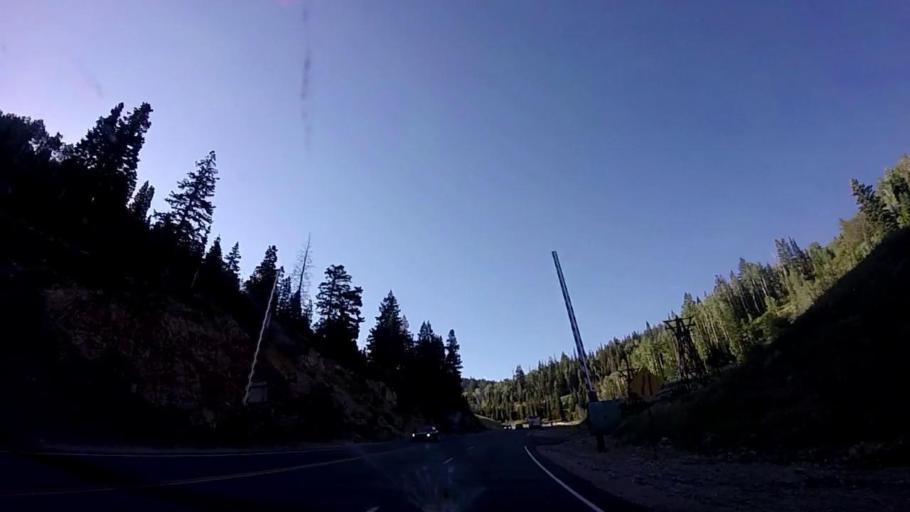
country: US
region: Utah
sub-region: Summit County
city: Park City
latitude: 40.6227
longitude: -111.4943
